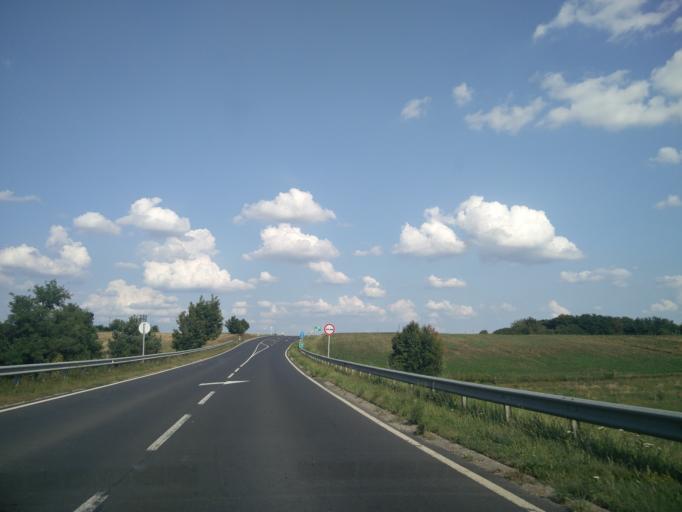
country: HU
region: Zala
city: Zalaegerszeg
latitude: 46.8815
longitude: 16.8221
